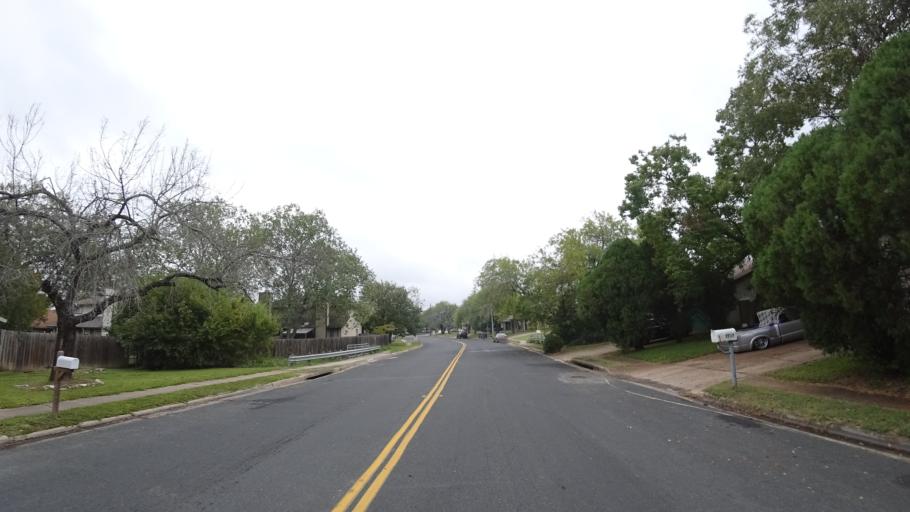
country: US
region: Texas
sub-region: Travis County
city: Shady Hollow
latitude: 30.2067
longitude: -97.8369
